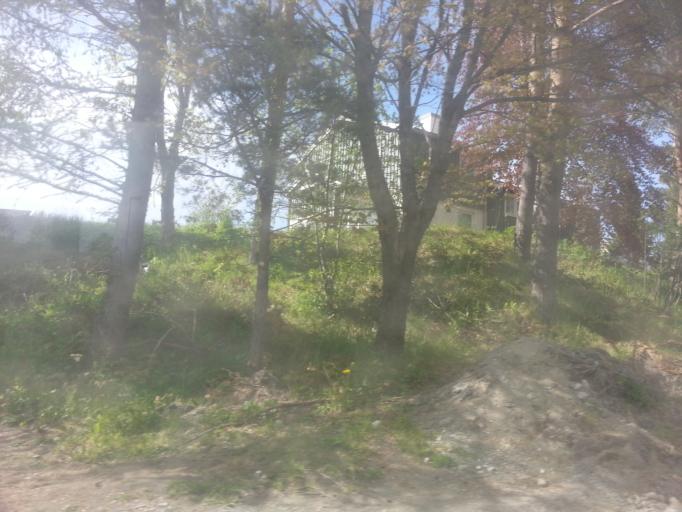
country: NO
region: Sor-Trondelag
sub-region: Trondheim
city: Trondheim
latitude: 63.4149
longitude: 10.4219
